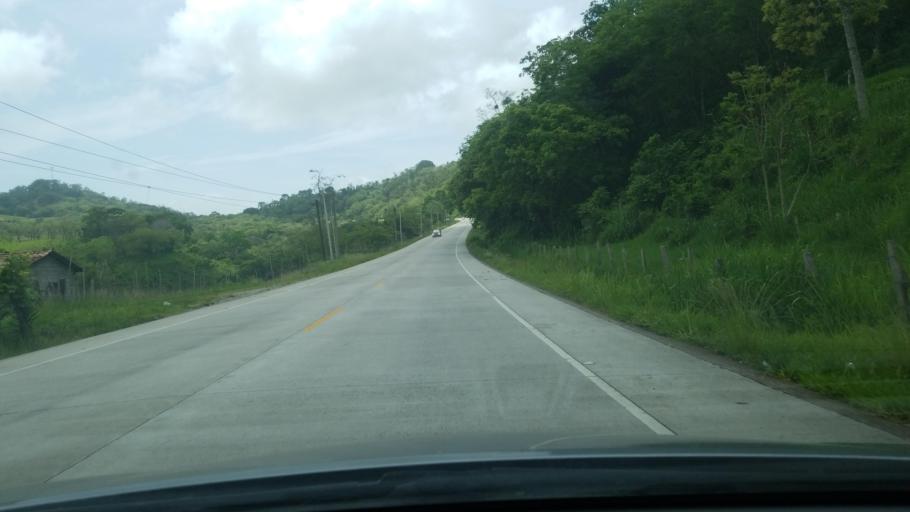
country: HN
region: Copan
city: Veracruz
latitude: 14.9234
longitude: -88.7639
